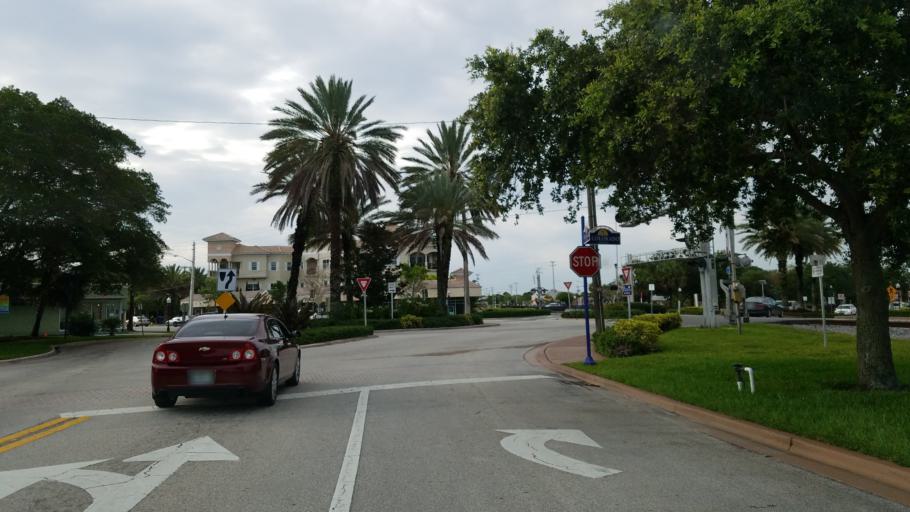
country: US
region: Florida
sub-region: Martin County
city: Stuart
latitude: 27.1980
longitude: -80.2530
